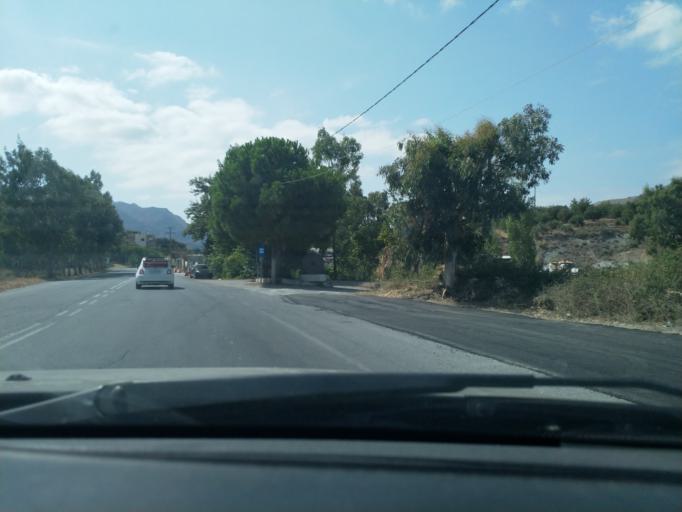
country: GR
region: Crete
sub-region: Nomos Rethymnis
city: Agia Foteini
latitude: 35.2214
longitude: 24.4995
